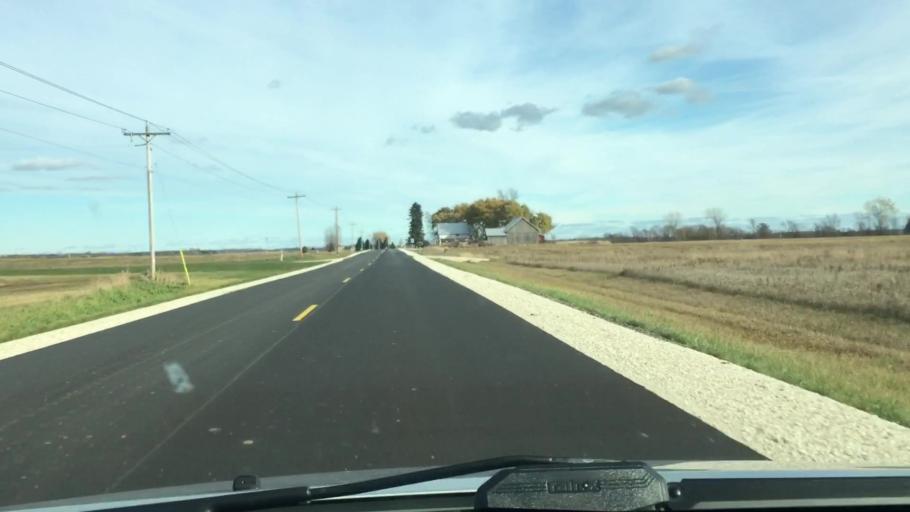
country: US
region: Wisconsin
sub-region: Kewaunee County
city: Algoma
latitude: 44.6898
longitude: -87.5156
